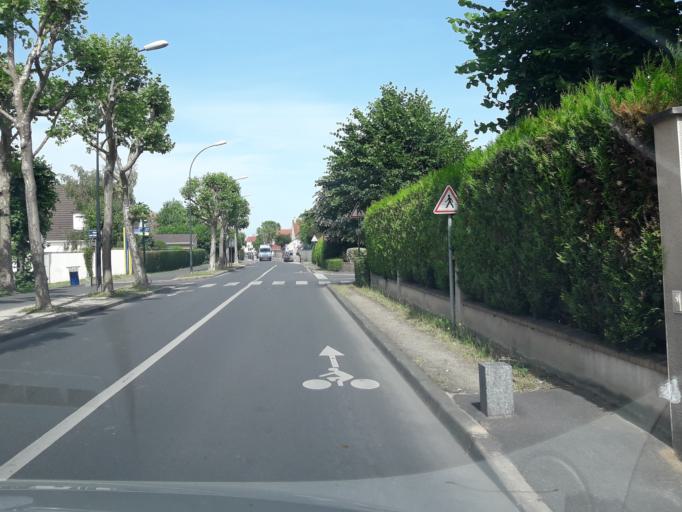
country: FR
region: Ile-de-France
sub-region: Departement de l'Essonne
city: Villemoisson-sur-Orge
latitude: 48.6596
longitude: 2.3303
